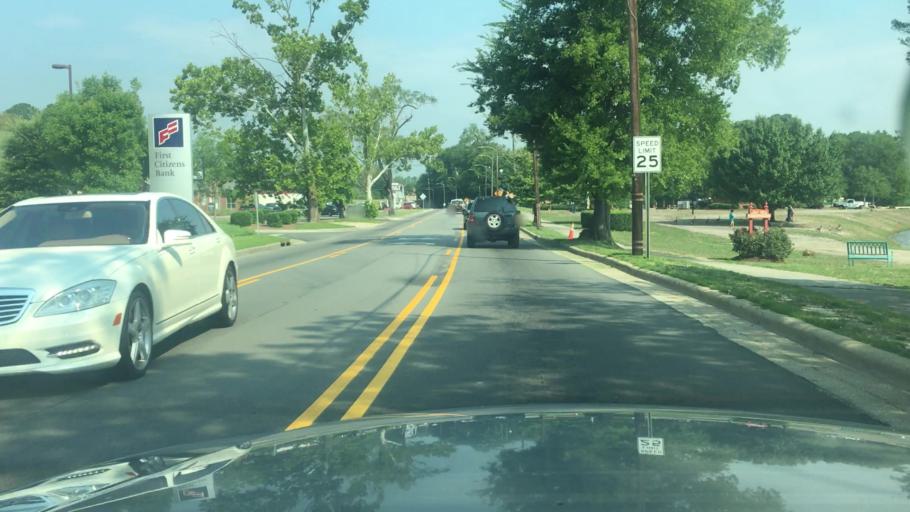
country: US
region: North Carolina
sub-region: Cumberland County
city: Hope Mills
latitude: 34.9726
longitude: -78.9463
